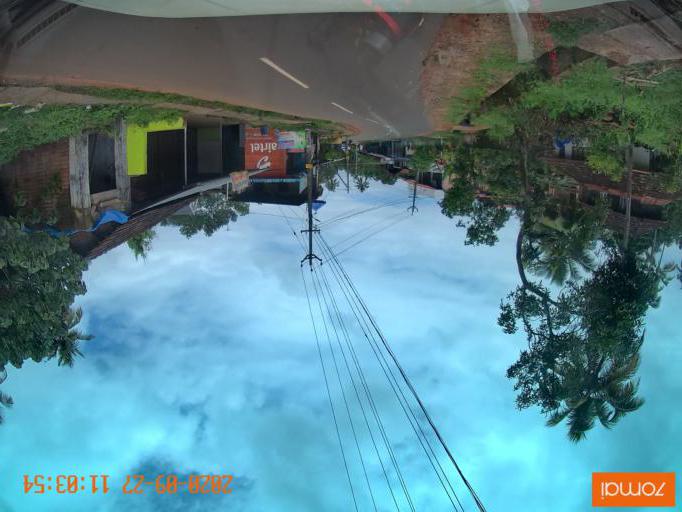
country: IN
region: Kerala
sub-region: Thrissur District
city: Irinjalakuda
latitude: 10.4224
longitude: 76.2528
